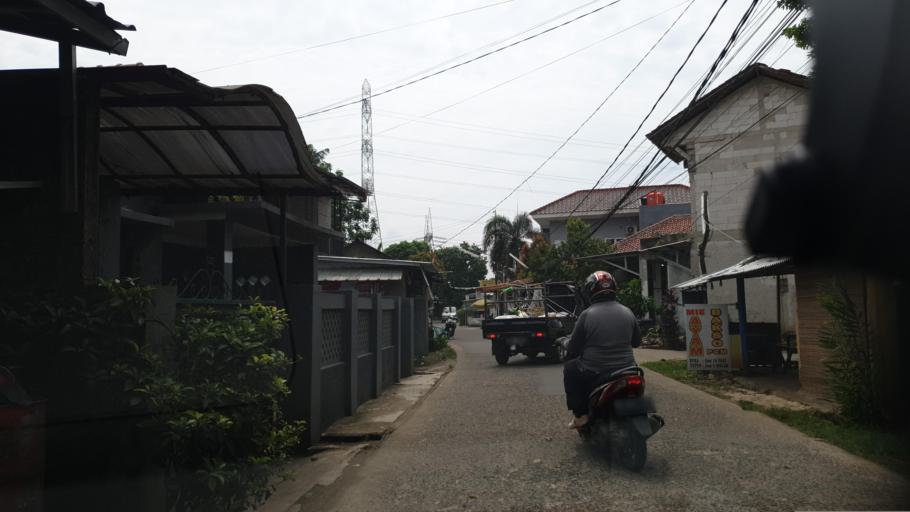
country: ID
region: West Java
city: Sawangan
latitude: -6.3792
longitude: 106.7604
